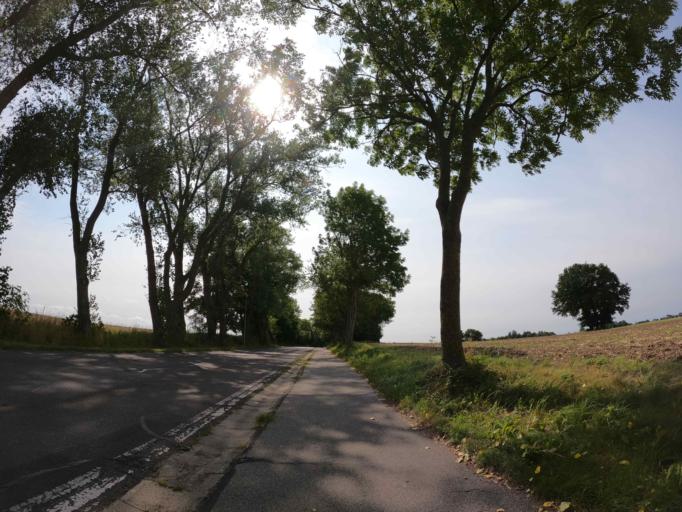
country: DE
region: Mecklenburg-Vorpommern
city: Kramerhof
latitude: 54.3471
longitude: 13.0691
